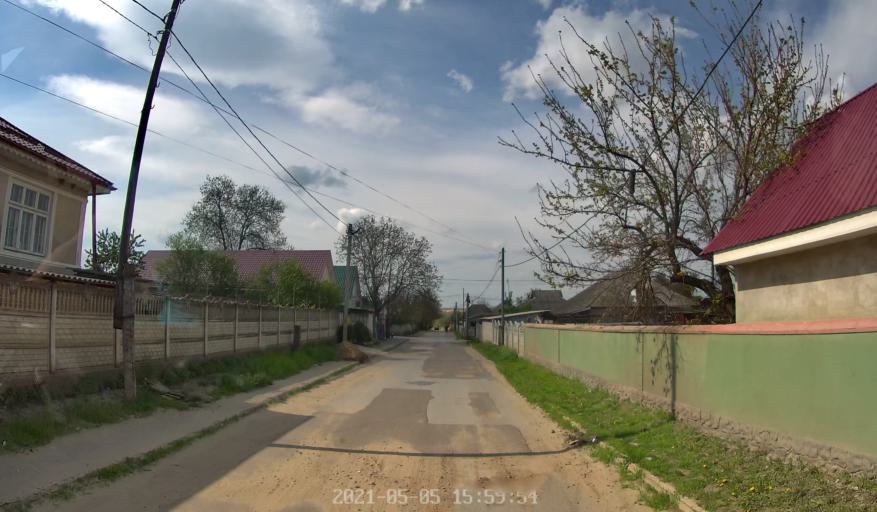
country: MD
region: Criuleni
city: Criuleni
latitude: 47.1419
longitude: 29.2012
